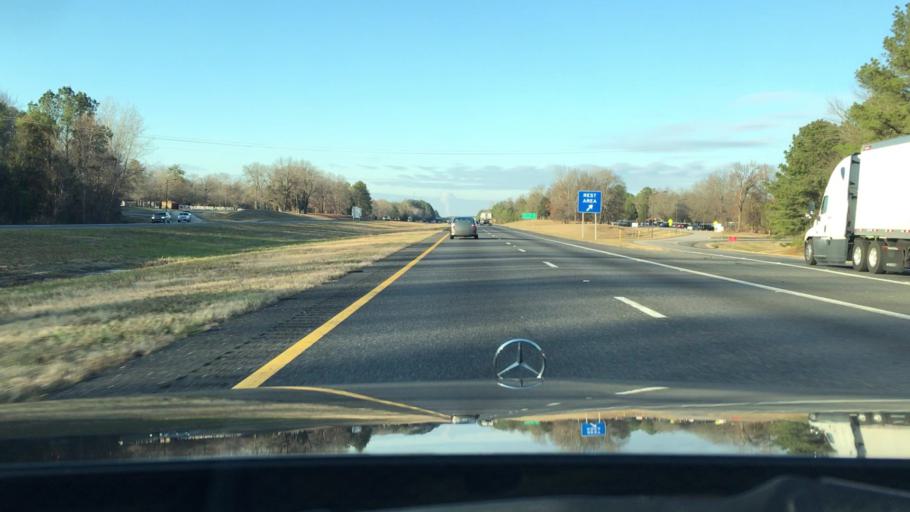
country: US
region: South Carolina
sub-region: York County
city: Lesslie
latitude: 34.7606
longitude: -81.0366
